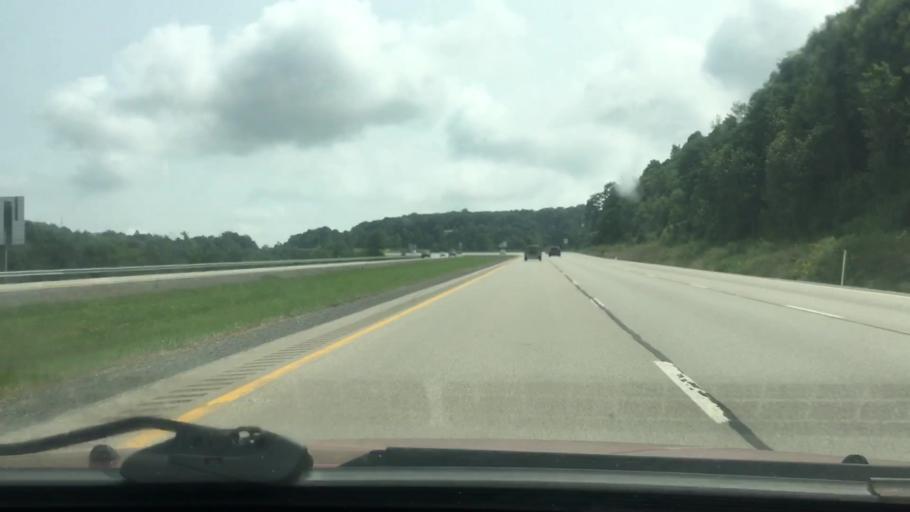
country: US
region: West Virginia
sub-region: Preston County
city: Terra Alta
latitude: 39.6593
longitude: -79.5023
